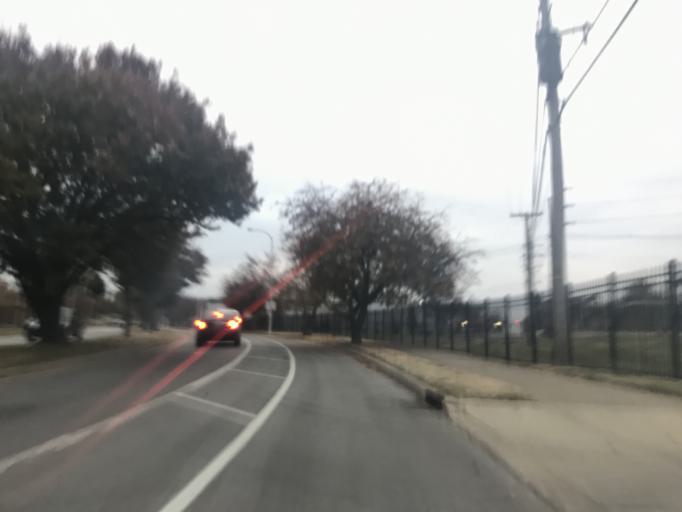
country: US
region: Kentucky
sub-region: Jefferson County
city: Louisville
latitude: 38.2501
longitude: -85.7730
